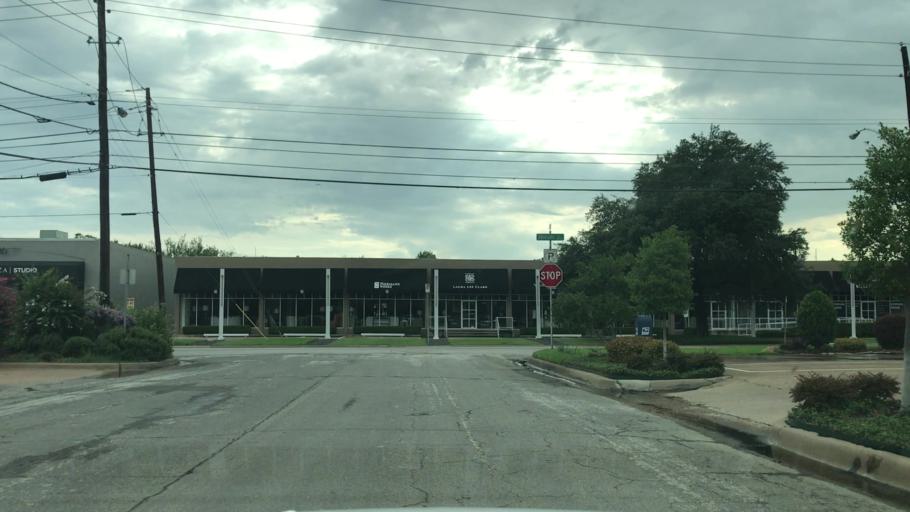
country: US
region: Texas
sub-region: Dallas County
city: Dallas
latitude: 32.7931
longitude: -96.8180
